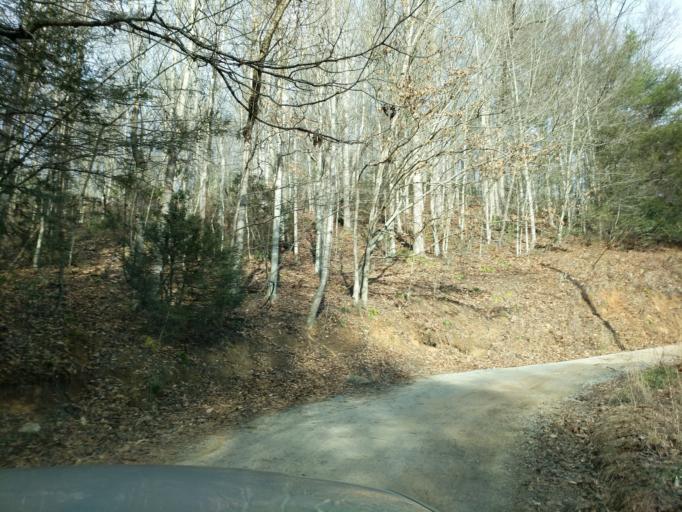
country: US
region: North Carolina
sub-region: Haywood County
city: Cove Creek
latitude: 35.6727
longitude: -83.0421
